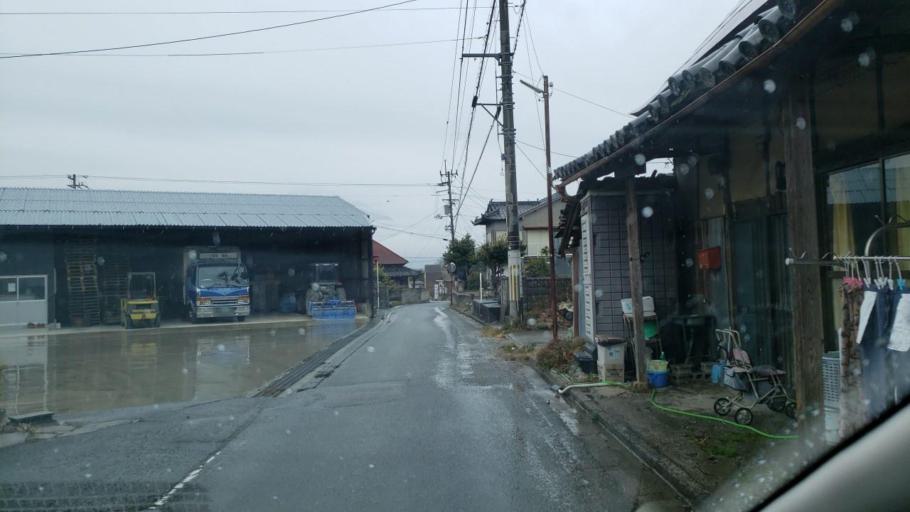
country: JP
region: Tokushima
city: Kamojimacho-jogejima
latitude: 34.0799
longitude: 134.2573
